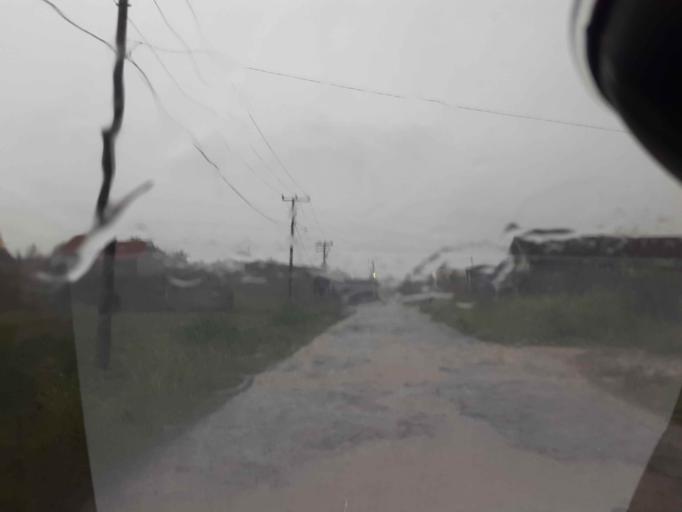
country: ID
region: Lampung
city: Kedaton
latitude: -5.3882
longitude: 105.3178
